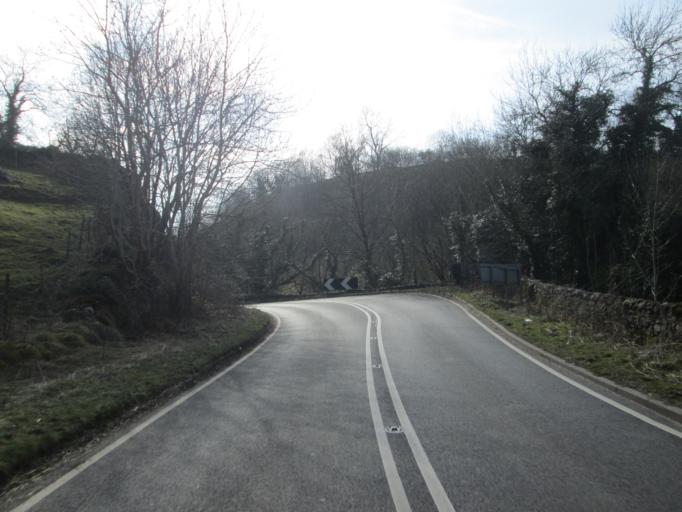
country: GB
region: England
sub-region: Derbyshire
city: Tideswell
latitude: 53.2539
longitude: -1.8019
